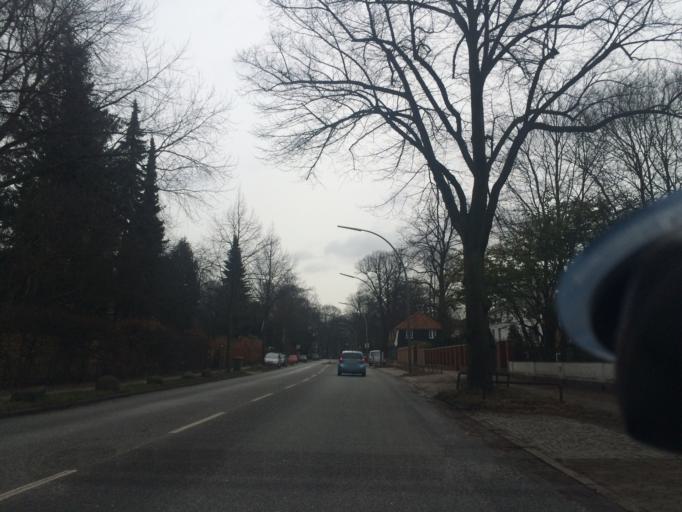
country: DE
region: Hamburg
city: Altona
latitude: 53.5462
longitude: 9.8968
